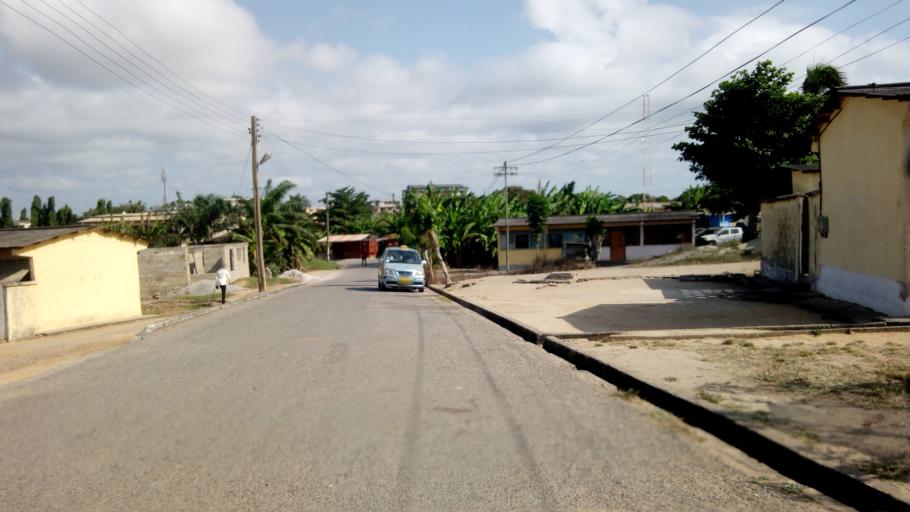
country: GH
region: Central
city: Cape Coast
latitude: 5.1178
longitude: -1.2679
